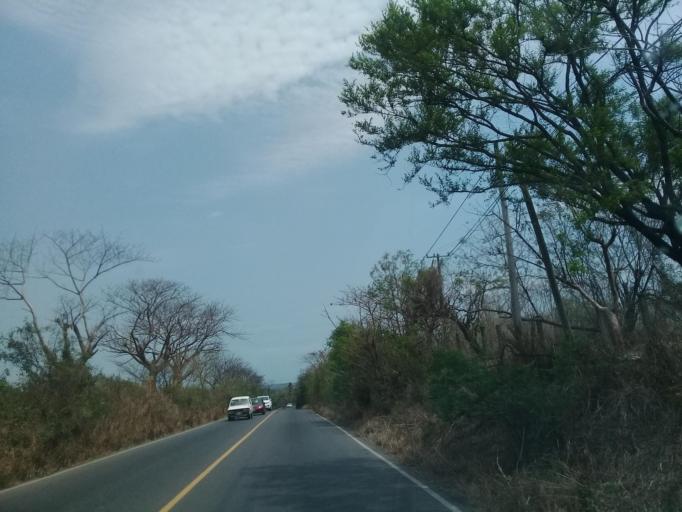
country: MX
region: Veracruz
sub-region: Veracruz
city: Delfino Victoria (Santa Fe)
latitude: 19.1655
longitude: -96.2870
